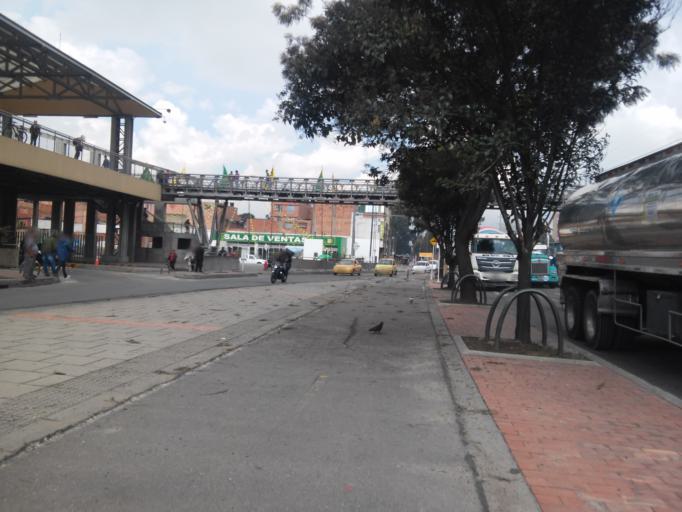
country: CO
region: Cundinamarca
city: Soacha
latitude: 4.5971
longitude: -74.1764
